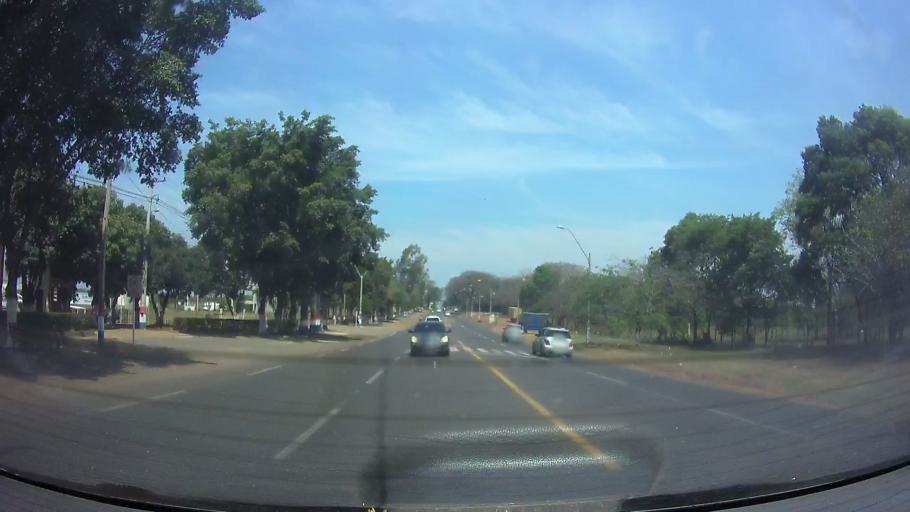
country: PY
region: Central
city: Capiata
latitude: -25.4039
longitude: -57.4629
